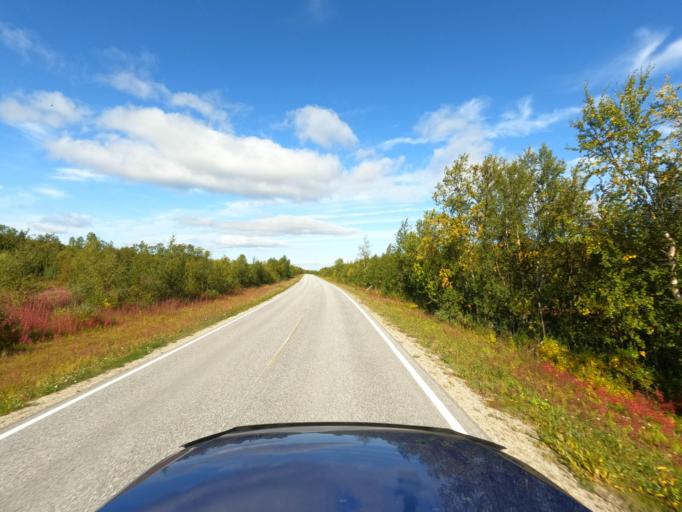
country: NO
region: Finnmark Fylke
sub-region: Karasjok
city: Karasjohka
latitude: 69.5995
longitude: 25.3292
